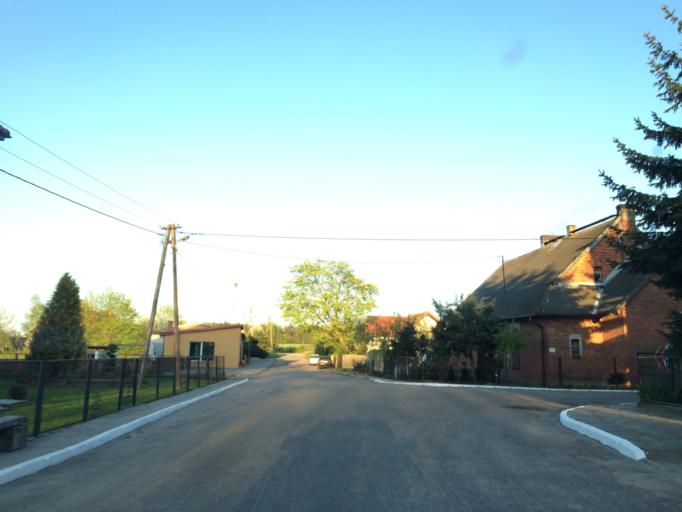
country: PL
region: Warmian-Masurian Voivodeship
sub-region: Powiat ilawski
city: Lubawa
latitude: 53.5255
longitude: 19.8749
